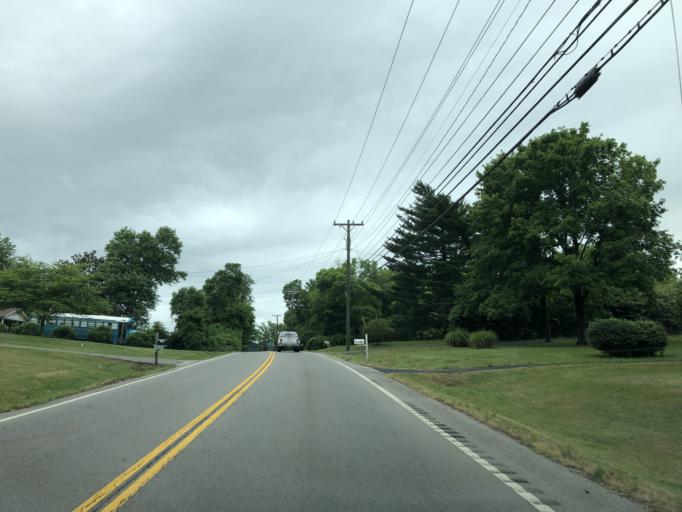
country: US
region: Tennessee
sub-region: Davidson County
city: Goodlettsville
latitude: 36.2757
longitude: -86.7658
